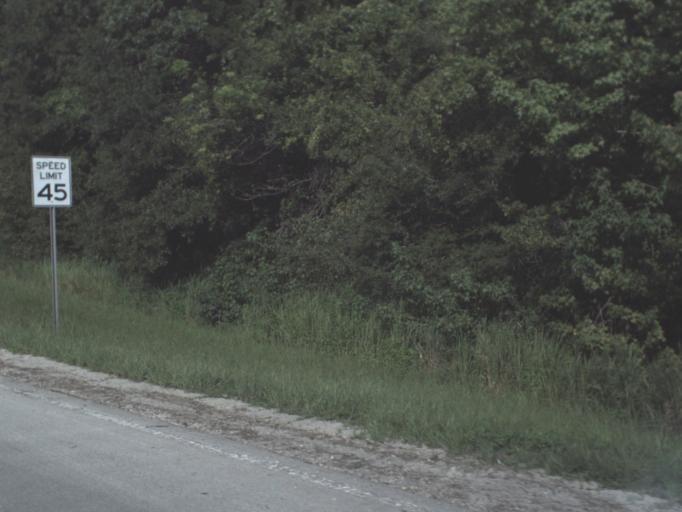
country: US
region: Florida
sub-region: Hernando County
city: North Brooksville
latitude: 28.5786
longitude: -82.4202
